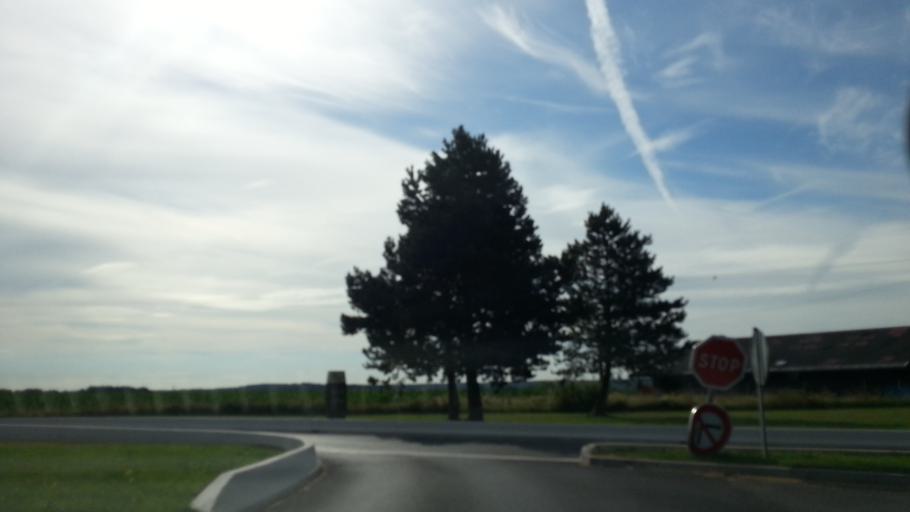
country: FR
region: Picardie
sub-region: Departement de l'Aisne
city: Fere-en-Tardenois
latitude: 49.1258
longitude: 3.5390
